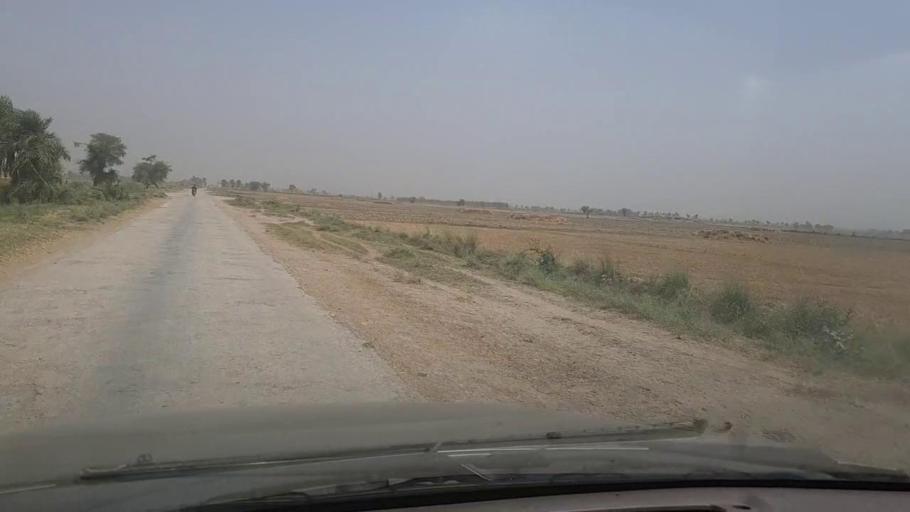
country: PK
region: Sindh
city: Madeji
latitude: 27.8099
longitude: 68.3979
